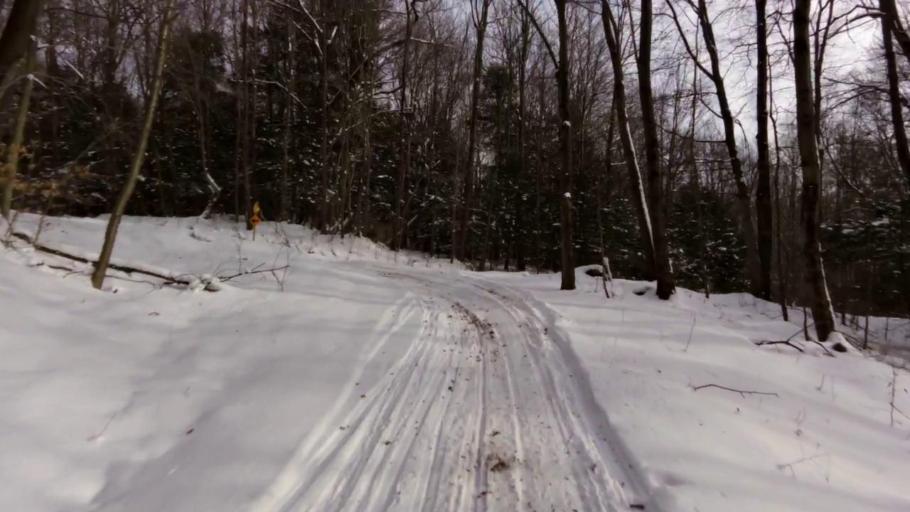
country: US
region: Pennsylvania
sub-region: McKean County
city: Foster Brook
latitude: 41.9993
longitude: -78.5330
